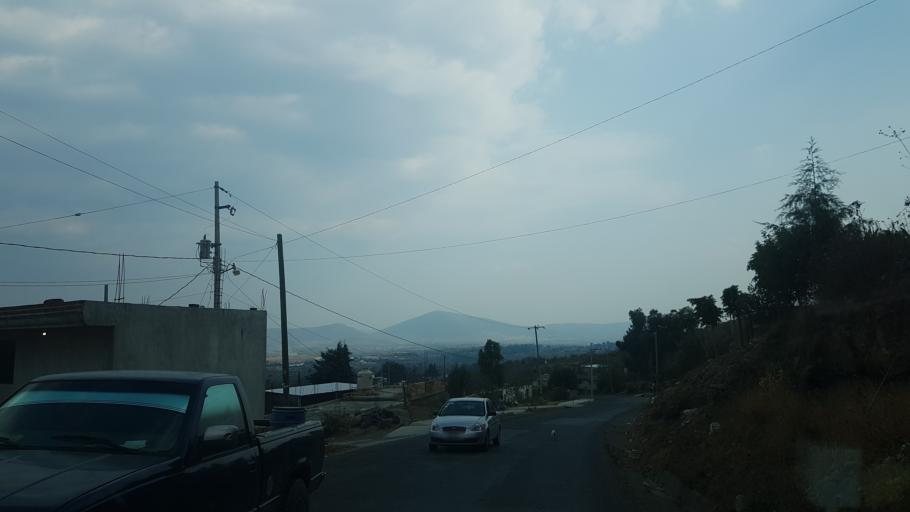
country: MX
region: Puebla
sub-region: Santa Isabel Cholula
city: San Martin Tlamapa
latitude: 18.9777
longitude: -98.3957
